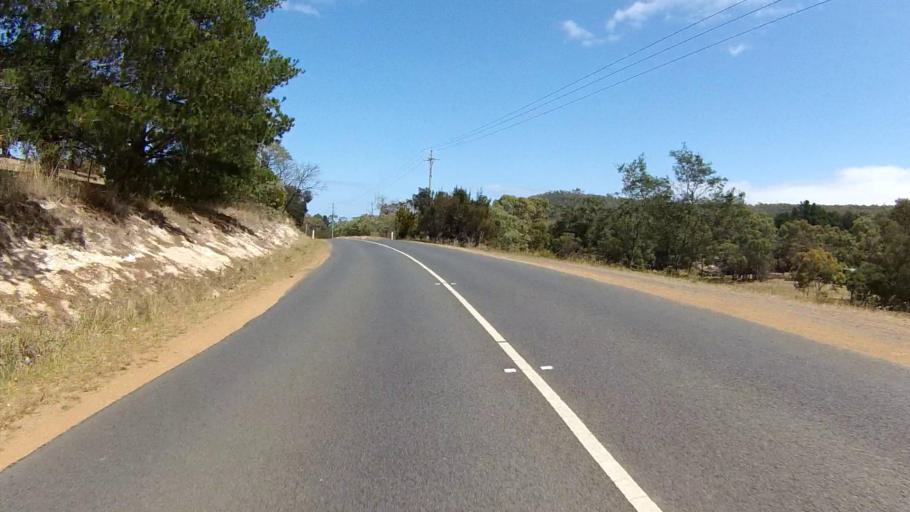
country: AU
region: Tasmania
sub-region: Clarence
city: Sandford
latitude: -42.9576
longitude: 147.4753
